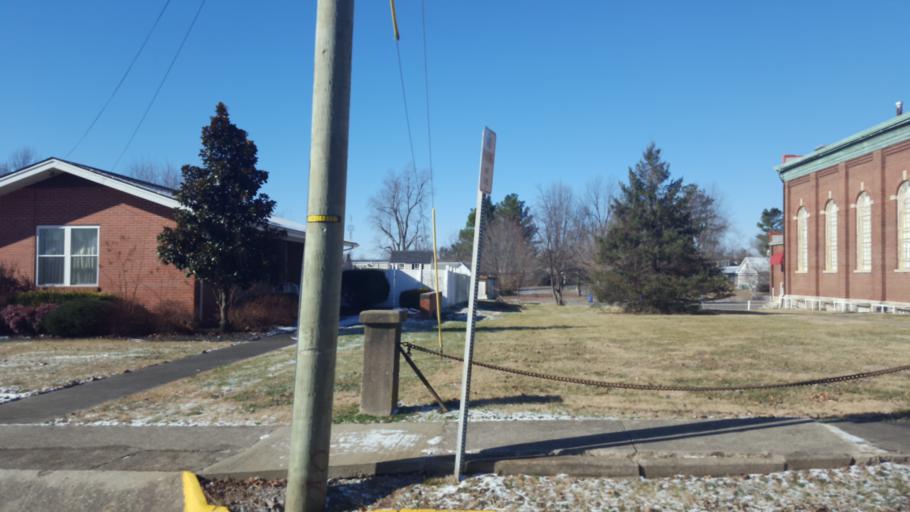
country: US
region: Kentucky
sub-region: Crittenden County
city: Marion
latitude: 37.3339
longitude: -88.0784
